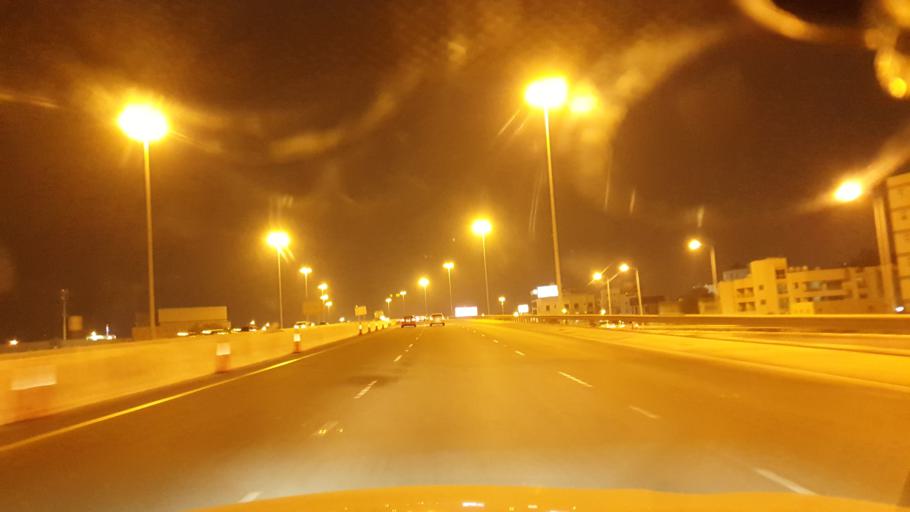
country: BH
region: Manama
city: Jidd Hafs
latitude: 26.2143
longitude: 50.5205
